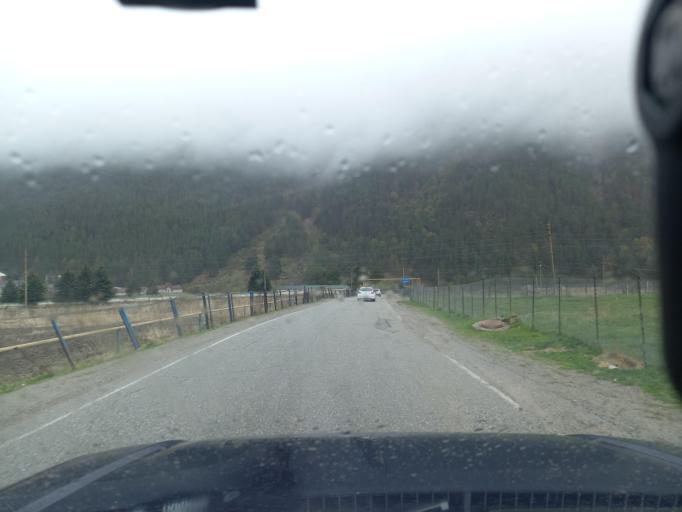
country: RU
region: Kabardino-Balkariya
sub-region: El'brusskiy Rayon
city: El'brus
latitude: 43.2584
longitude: 42.6463
